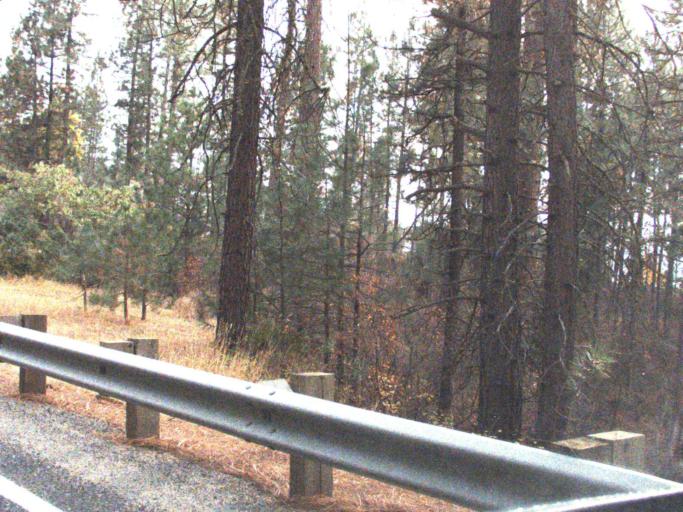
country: US
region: Washington
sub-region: Stevens County
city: Kettle Falls
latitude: 48.3093
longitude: -118.1479
